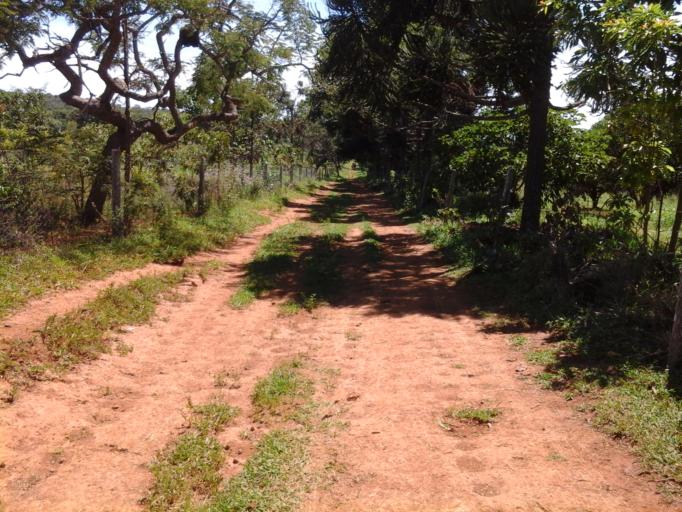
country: BR
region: Goias
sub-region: Abadiania
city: Abadiania
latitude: -15.9803
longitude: -48.5347
